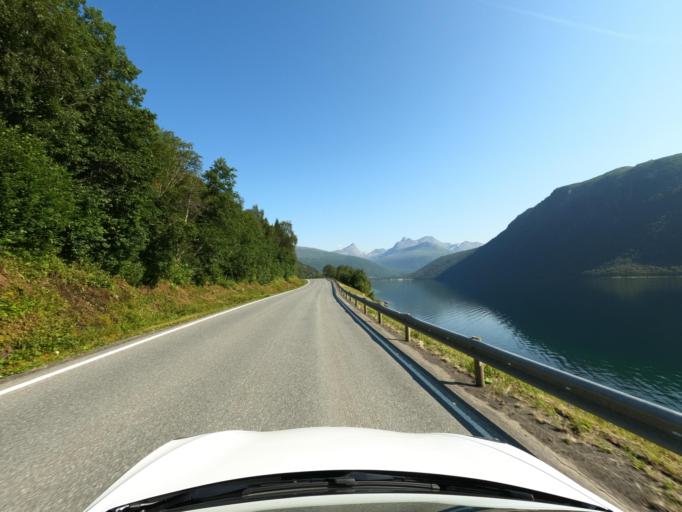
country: NO
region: Nordland
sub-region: Narvik
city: Narvik
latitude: 68.3952
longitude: 17.5220
